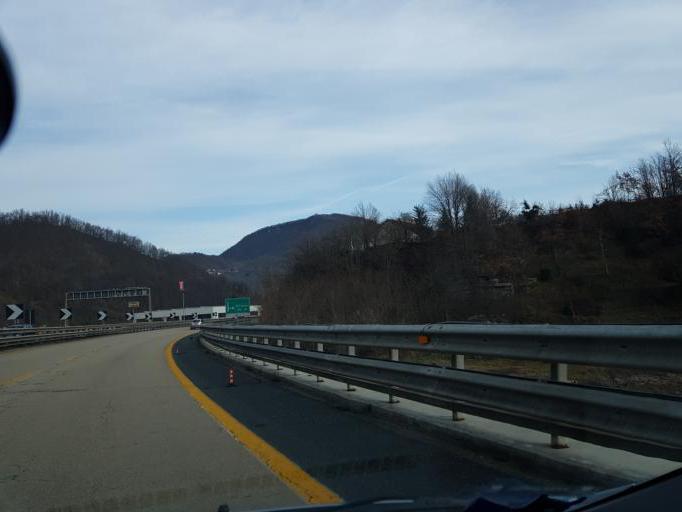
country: IT
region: Liguria
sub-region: Provincia di Genova
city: Ronco Scrivia
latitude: 44.6021
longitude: 8.9513
